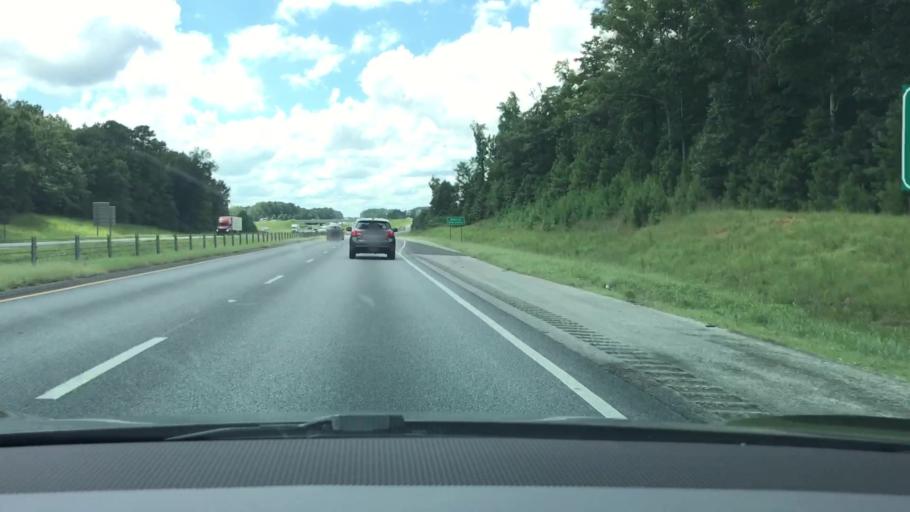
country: US
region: Alabama
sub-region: Lee County
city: Opelika
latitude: 32.6085
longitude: -85.4209
